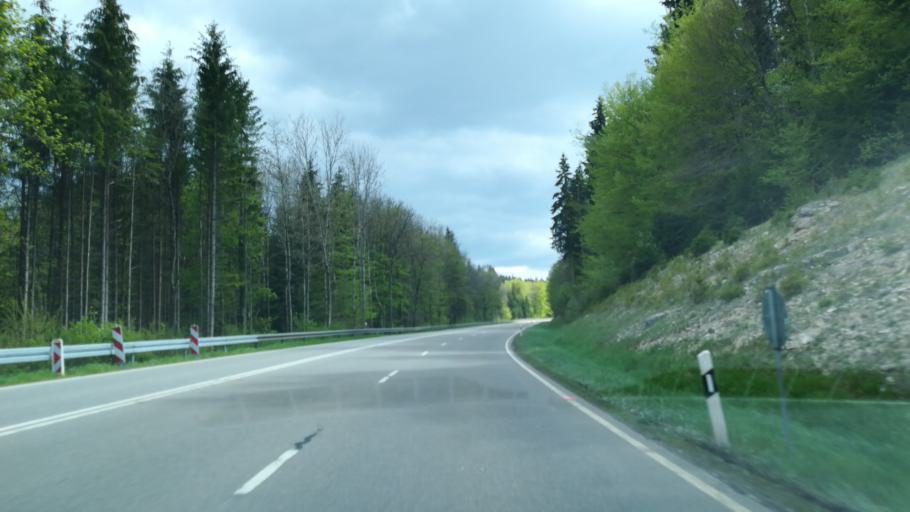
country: DE
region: Baden-Wuerttemberg
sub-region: Freiburg Region
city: Blumberg
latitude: 47.8326
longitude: 8.5639
